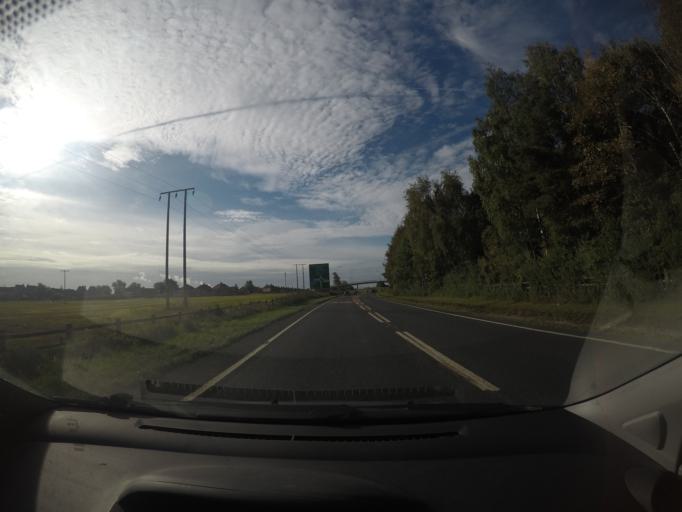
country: GB
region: England
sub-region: North Yorkshire
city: Barlby
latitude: 53.7992
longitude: -1.0357
